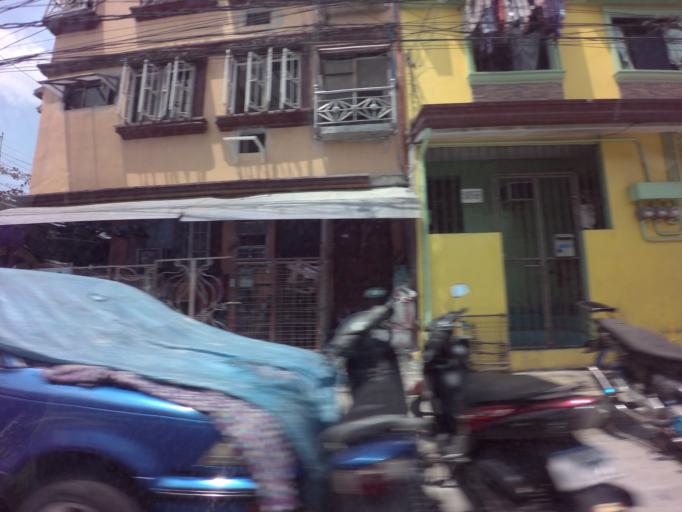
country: PH
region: Metro Manila
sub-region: Mandaluyong
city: Mandaluyong City
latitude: 14.5731
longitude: 121.0227
